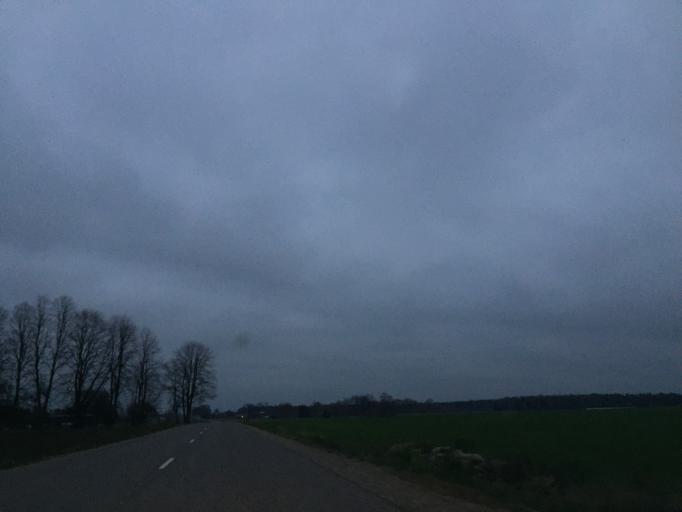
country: LV
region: Koceni
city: Koceni
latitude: 57.5480
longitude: 25.2852
